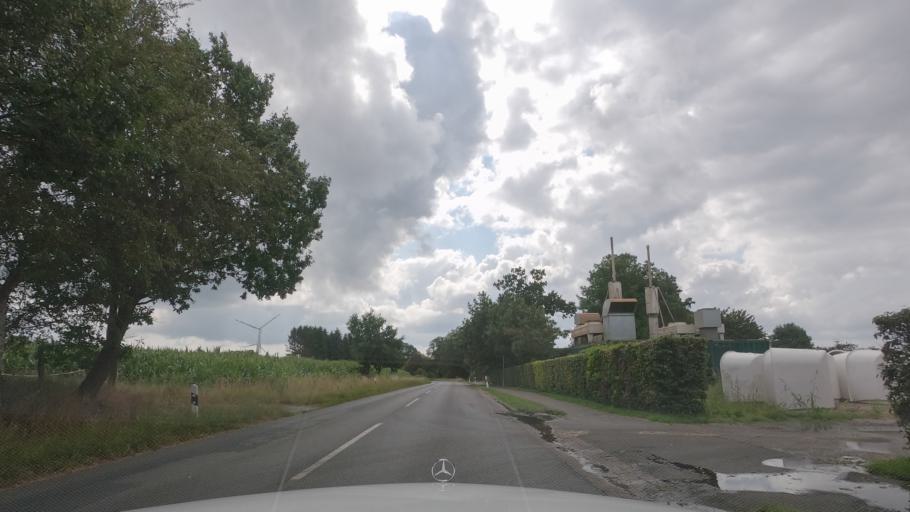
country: DE
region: Lower Saxony
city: Uthlede
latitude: 53.3067
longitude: 8.5812
